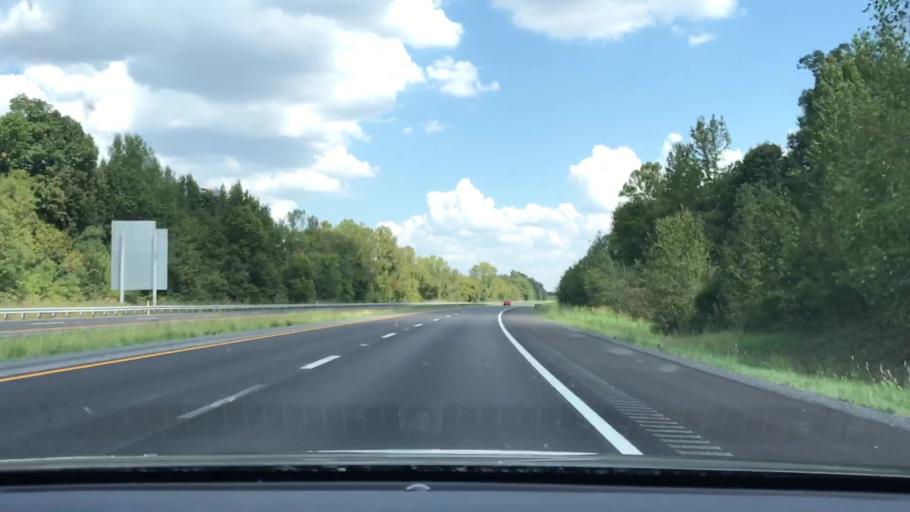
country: US
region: Kentucky
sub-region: Lyon County
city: Eddyville
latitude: 37.0826
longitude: -88.0705
